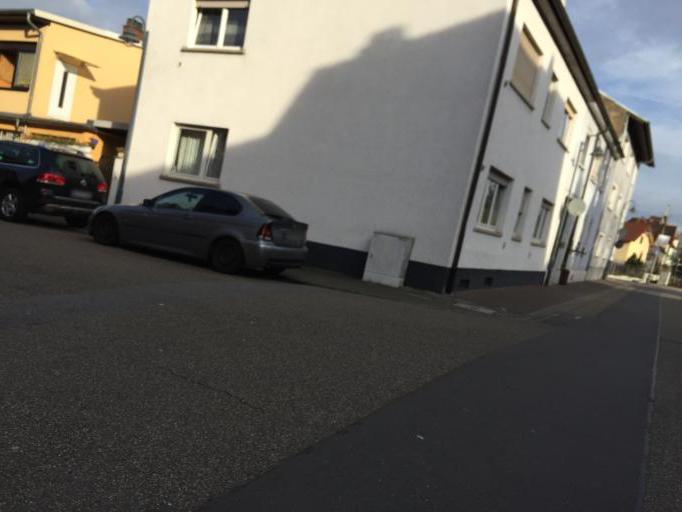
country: DE
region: Baden-Wuerttemberg
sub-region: Karlsruhe Region
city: Schwetzingen
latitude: 49.3877
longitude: 8.5762
